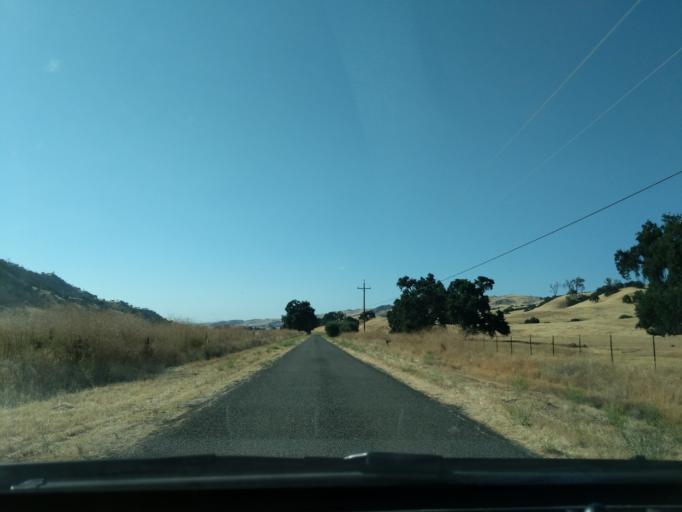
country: US
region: California
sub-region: Monterey County
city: King City
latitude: 36.1362
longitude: -120.7484
